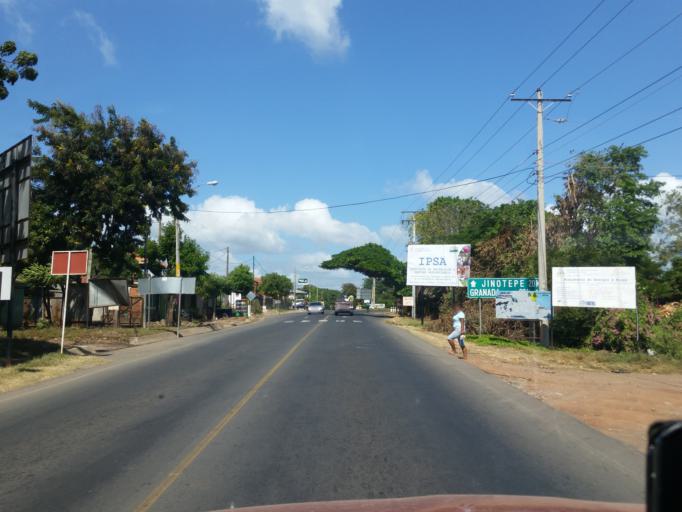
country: NI
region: Granada
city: Nandaime
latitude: 11.7755
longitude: -86.0528
